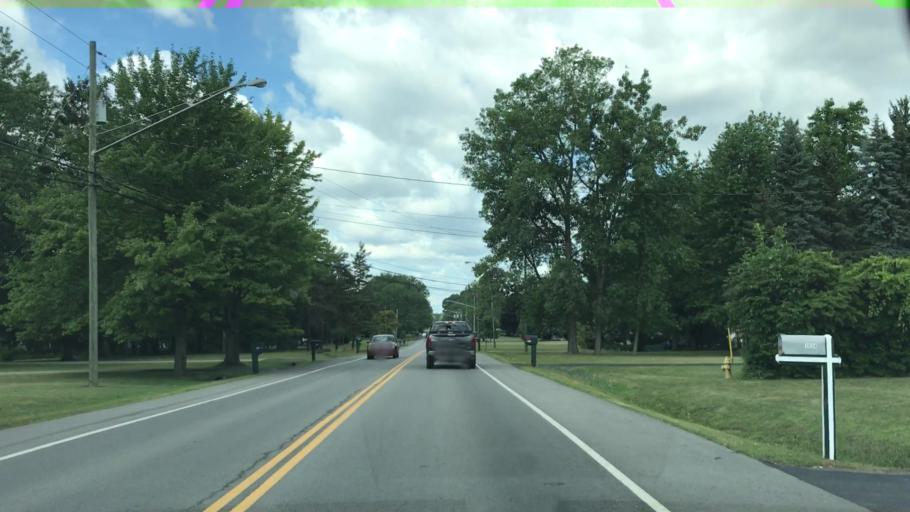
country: US
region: New York
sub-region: Erie County
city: Depew
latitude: 42.8924
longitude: -78.7030
